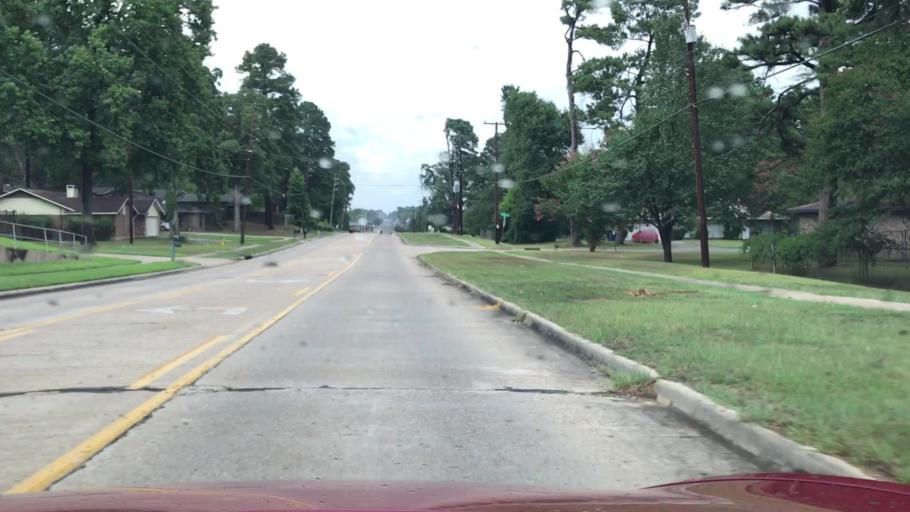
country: US
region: Louisiana
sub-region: De Soto Parish
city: Stonewall
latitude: 32.3967
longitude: -93.7804
